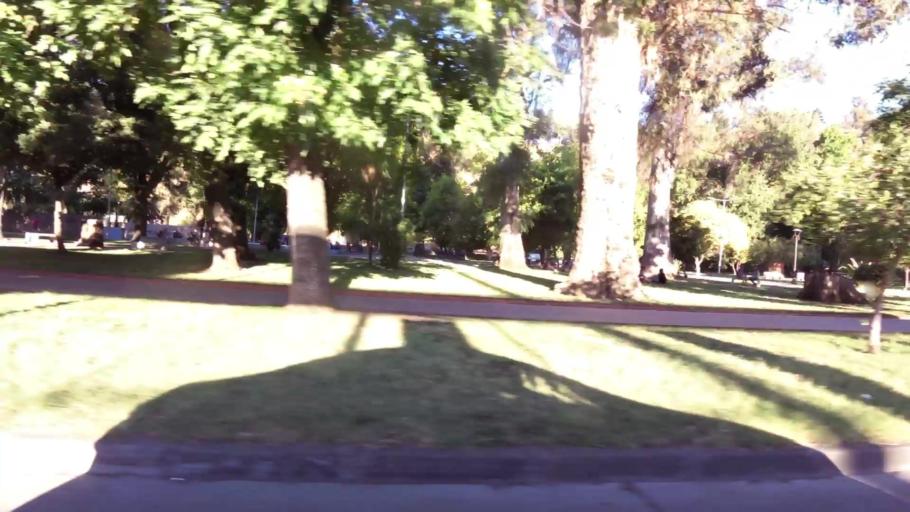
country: CL
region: Maule
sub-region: Provincia de Curico
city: Curico
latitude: -34.9815
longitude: -71.2347
